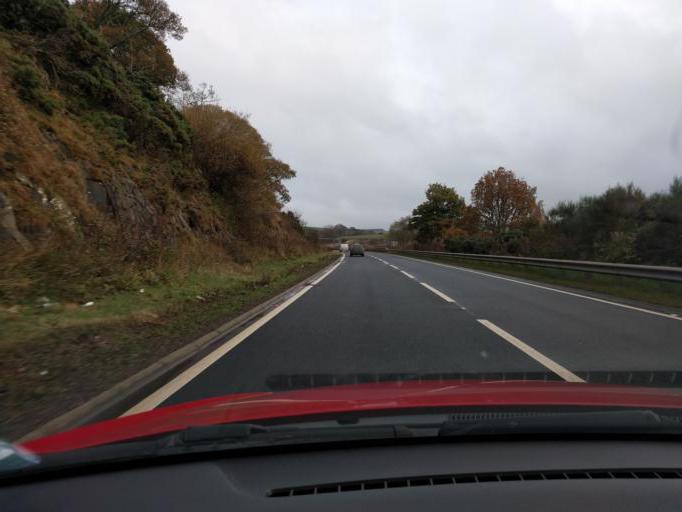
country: GB
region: Scotland
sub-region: The Scottish Borders
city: Duns
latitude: 55.8840
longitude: -2.3148
